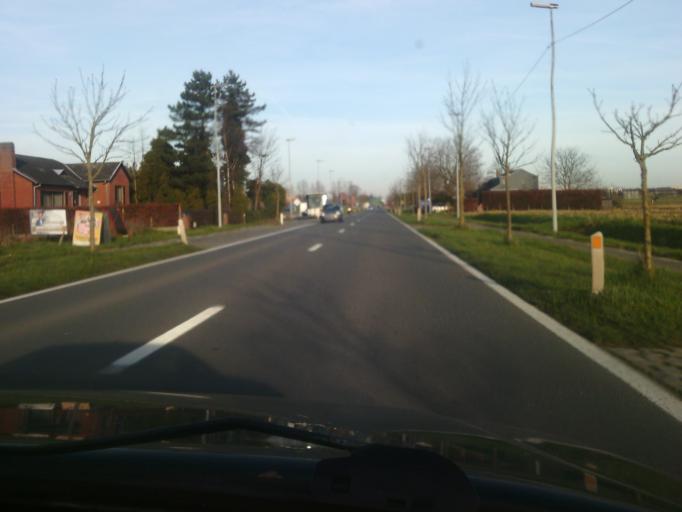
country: BE
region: Flanders
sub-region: Provincie Oost-Vlaanderen
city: Berlare
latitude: 51.0159
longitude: 4.0381
